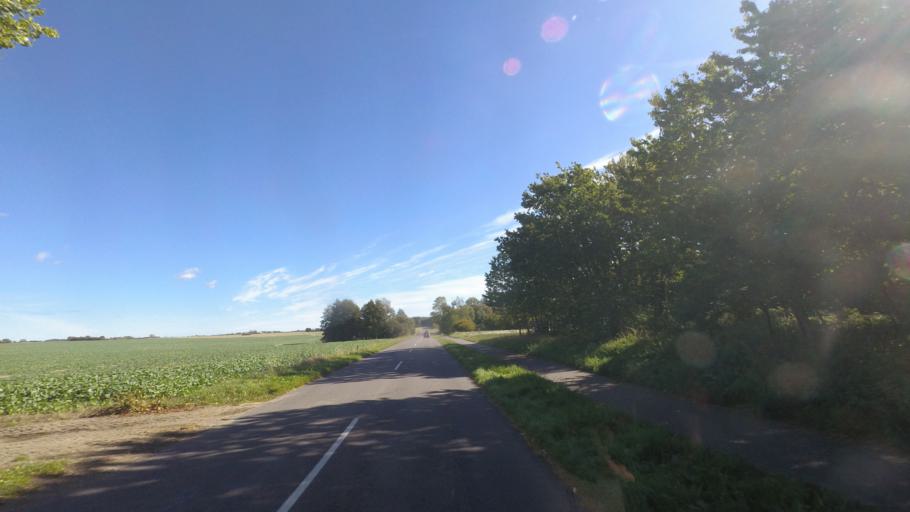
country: DK
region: Capital Region
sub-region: Bornholm Kommune
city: Nexo
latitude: 55.0026
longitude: 15.0458
